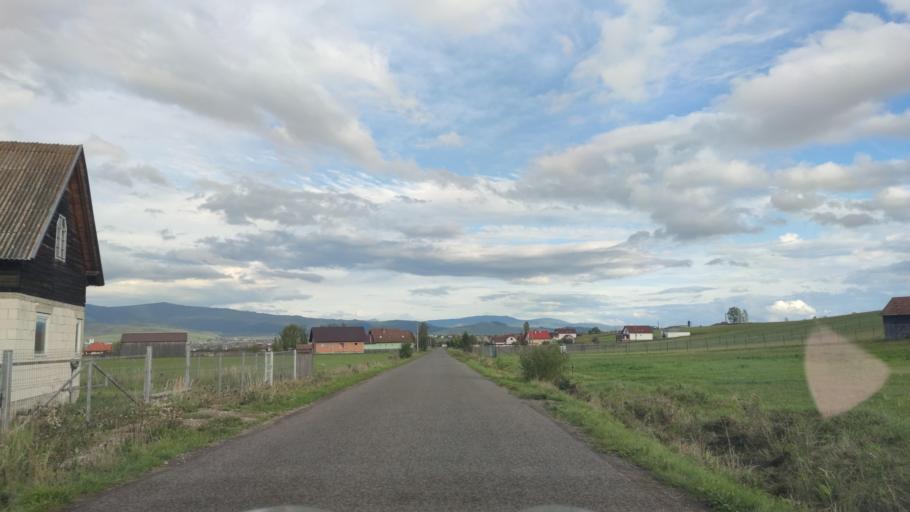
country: RO
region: Harghita
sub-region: Comuna Remetea
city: Remetea
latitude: 46.8035
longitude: 25.4340
